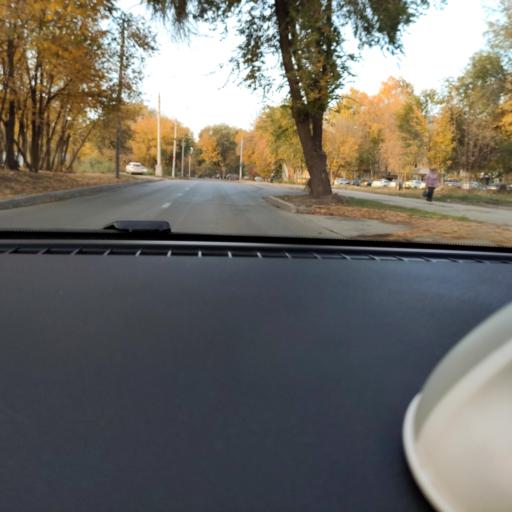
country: RU
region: Samara
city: Samara
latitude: 53.2357
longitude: 50.2343
